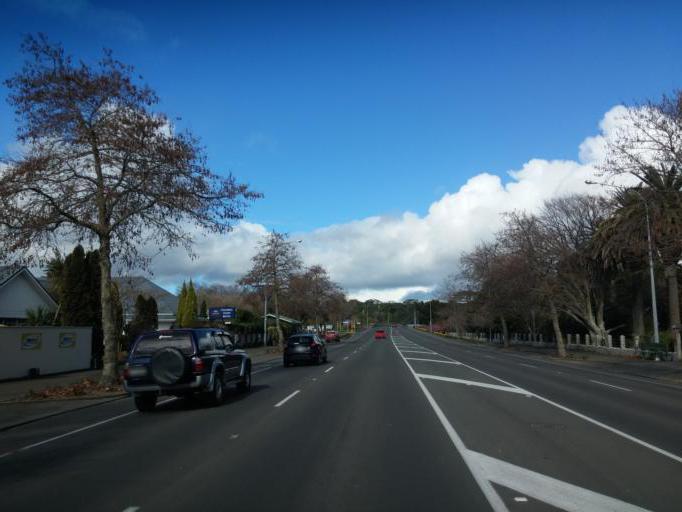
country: NZ
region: Manawatu-Wanganui
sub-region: Palmerston North City
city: Palmerston North
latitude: -40.3706
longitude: 175.6223
